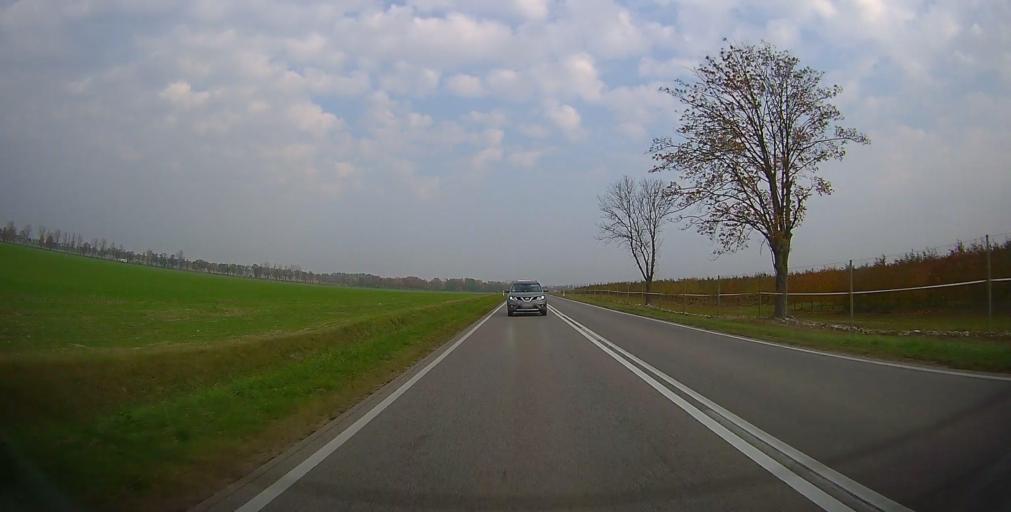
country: PL
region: Masovian Voivodeship
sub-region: Powiat grojecki
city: Belsk Duzy
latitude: 51.8019
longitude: 20.7898
